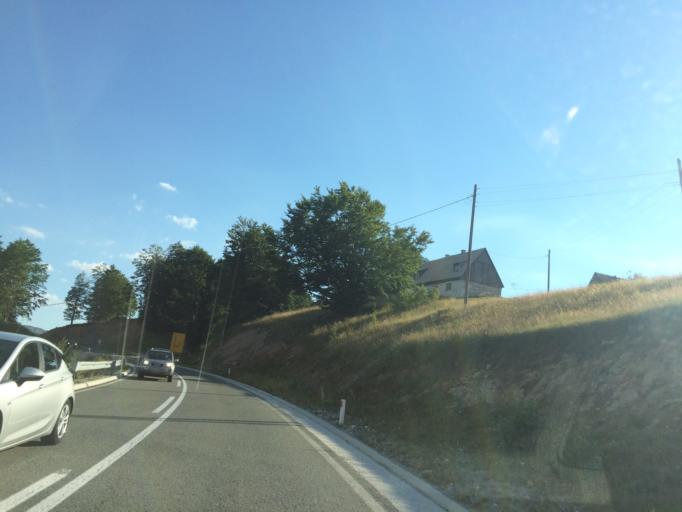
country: ME
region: Opstina Zabljak
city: Zabljak
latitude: 43.0998
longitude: 19.1112
